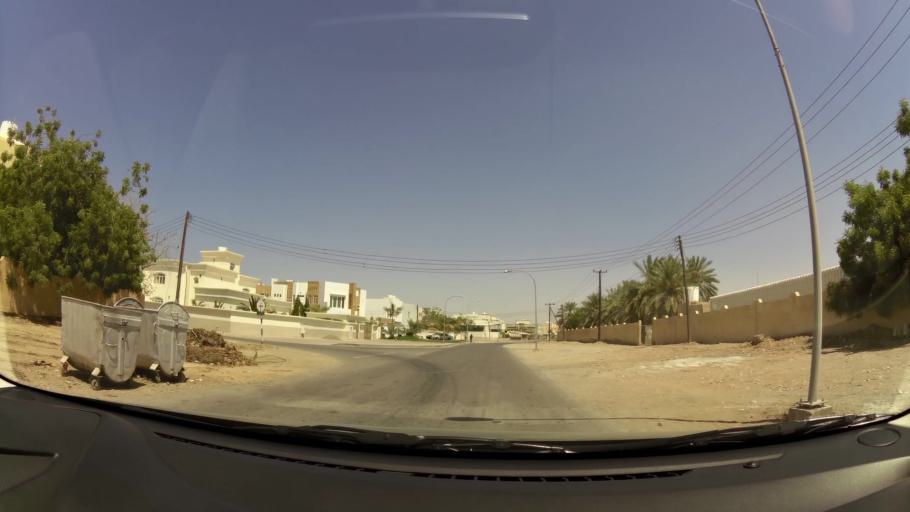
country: OM
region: Muhafazat Masqat
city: As Sib al Jadidah
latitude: 23.6280
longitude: 58.2259
